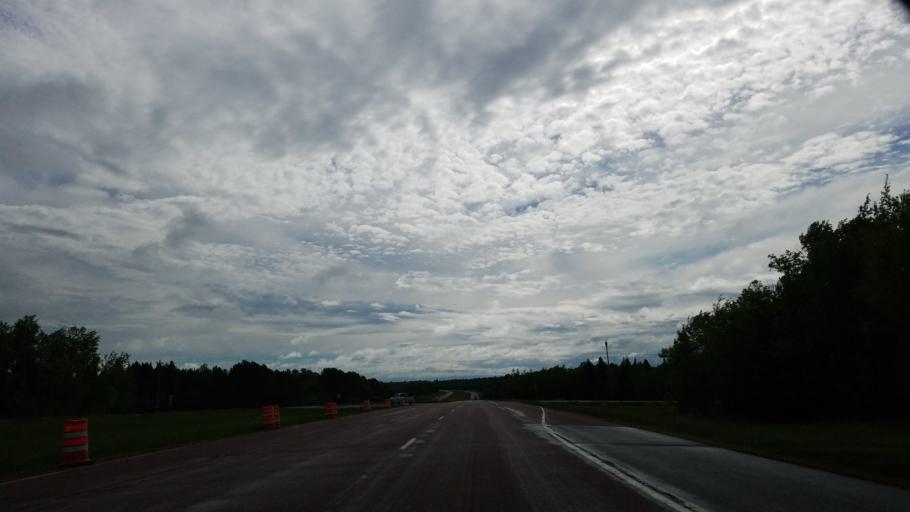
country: US
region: Minnesota
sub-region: Lake County
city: Two Harbors
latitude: 46.9278
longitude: -91.8494
